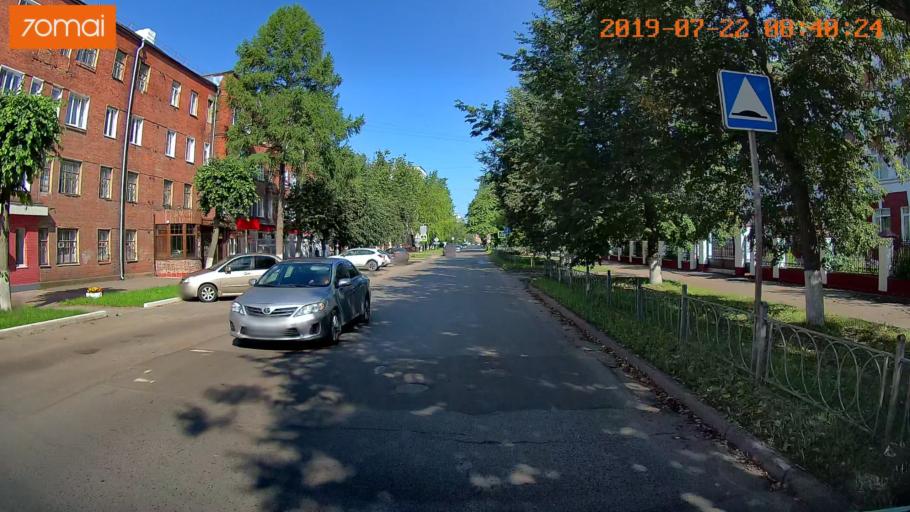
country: RU
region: Ivanovo
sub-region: Gorod Ivanovo
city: Ivanovo
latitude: 56.9976
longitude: 40.9880
